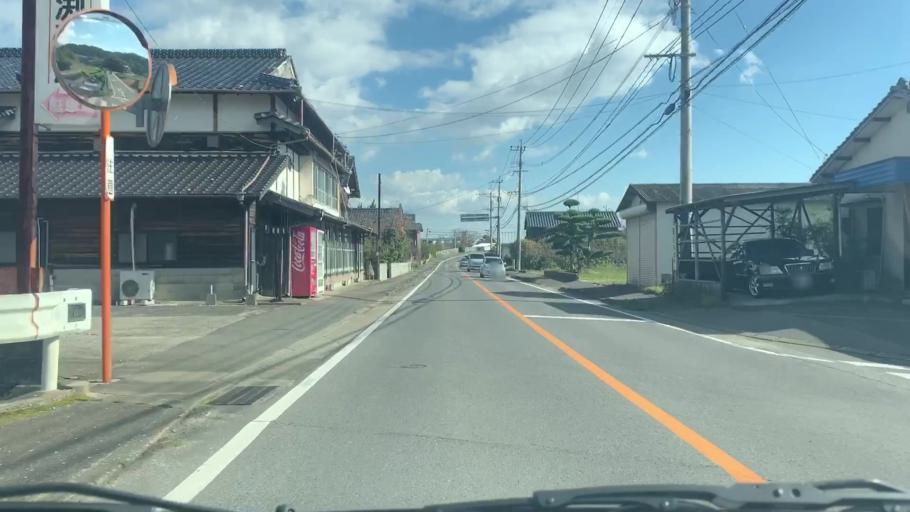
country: JP
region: Saga Prefecture
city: Saga-shi
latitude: 33.2718
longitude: 130.1842
